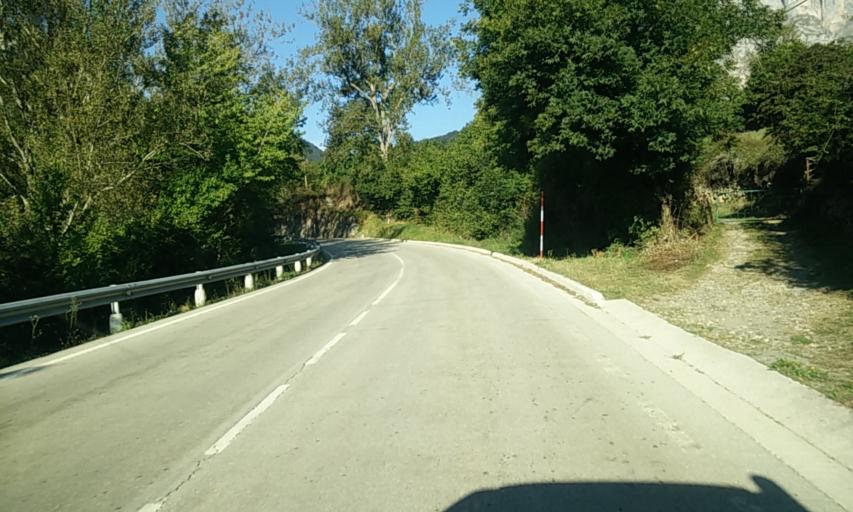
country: ES
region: Cantabria
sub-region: Provincia de Cantabria
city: Camaleno
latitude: 43.1309
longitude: -4.8003
